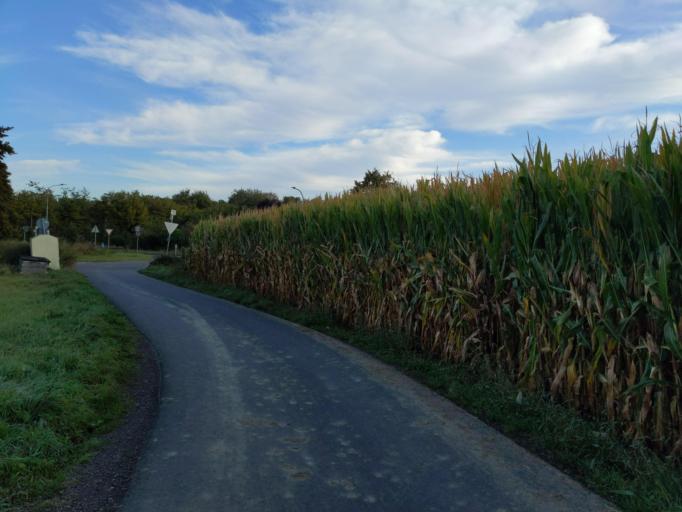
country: DE
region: North Rhine-Westphalia
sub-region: Regierungsbezirk Dusseldorf
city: Kaarst
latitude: 51.2195
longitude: 6.5946
